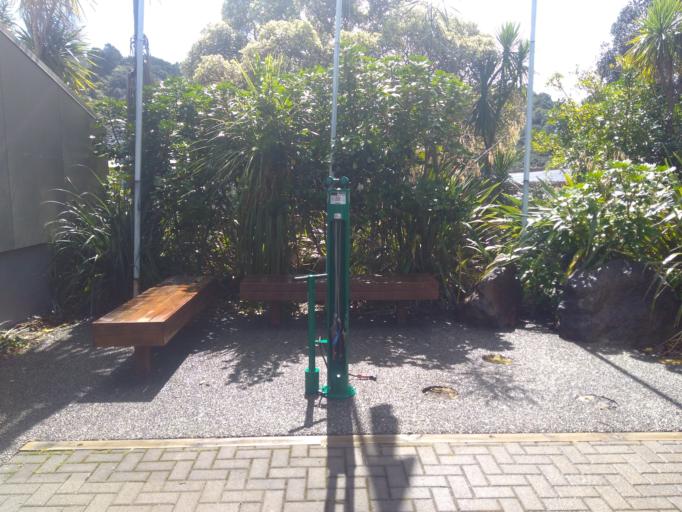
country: NZ
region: Bay of Plenty
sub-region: Western Bay of Plenty District
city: Waihi Beach
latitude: -37.3979
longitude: 175.9371
